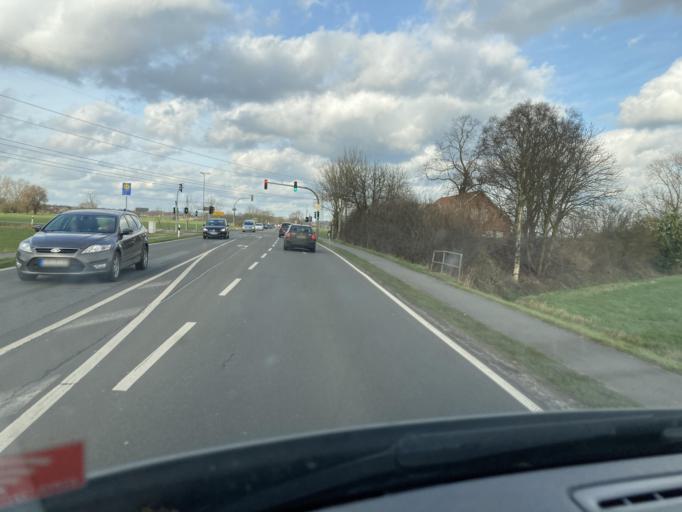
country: DE
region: Lower Saxony
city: Leer
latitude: 53.2091
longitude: 7.4818
